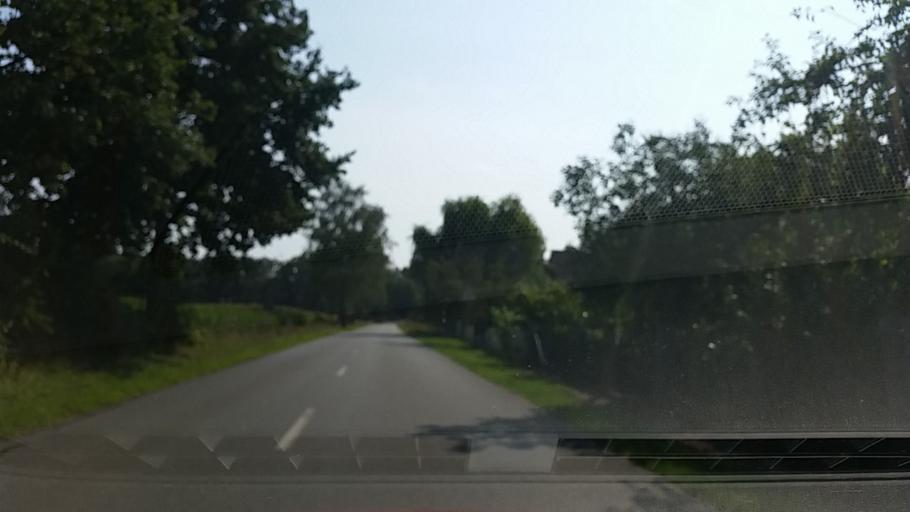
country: DE
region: Mecklenburg-Vorpommern
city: Domitz
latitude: 53.1293
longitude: 11.2346
